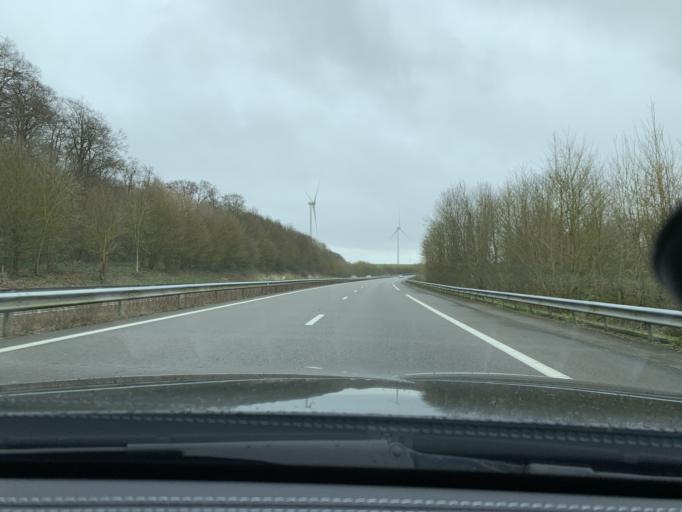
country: FR
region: Picardie
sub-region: Departement de l'Oise
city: Breteuil
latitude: 49.6488
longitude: 2.2162
